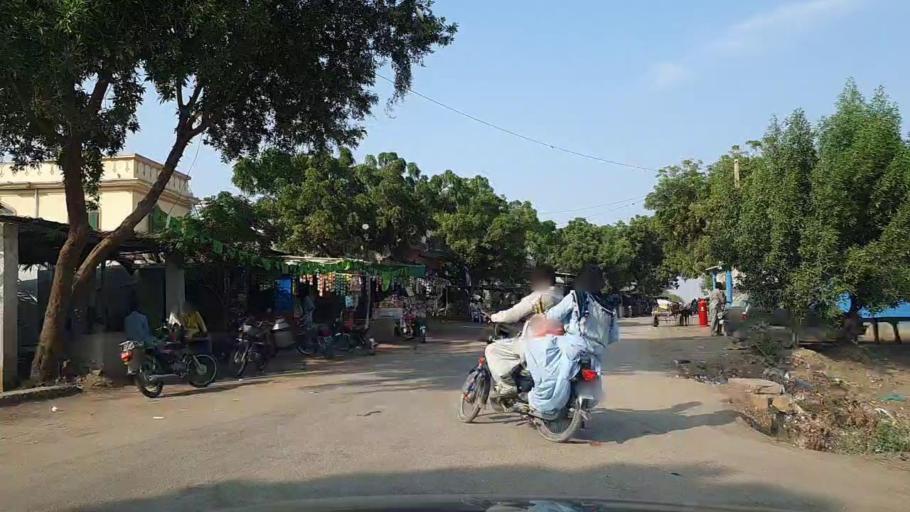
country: PK
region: Sindh
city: Thatta
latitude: 24.6500
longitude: 67.9108
